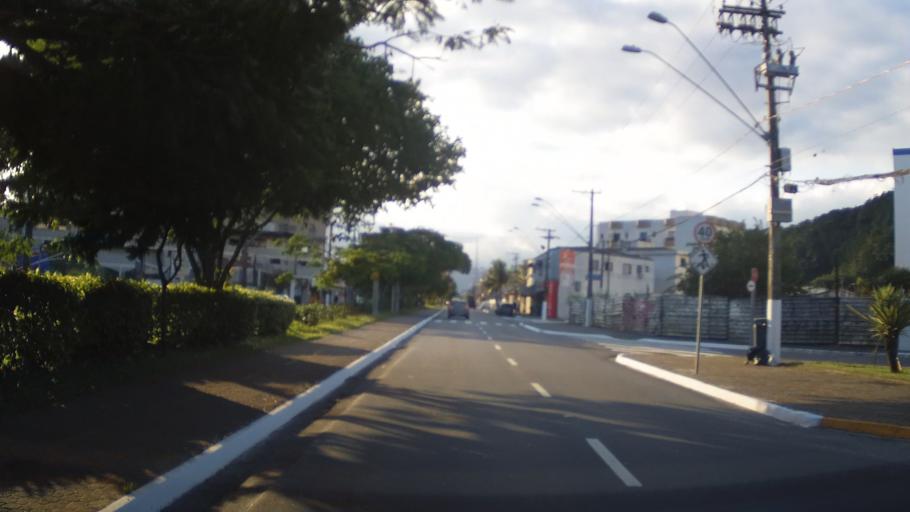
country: BR
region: Sao Paulo
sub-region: Praia Grande
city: Praia Grande
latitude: -24.0063
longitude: -46.4071
